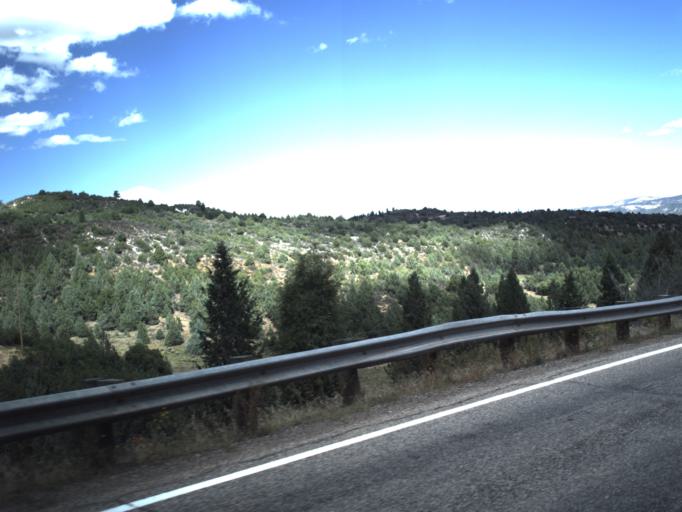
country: US
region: Utah
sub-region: Garfield County
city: Panguitch
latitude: 37.4906
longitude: -112.5289
